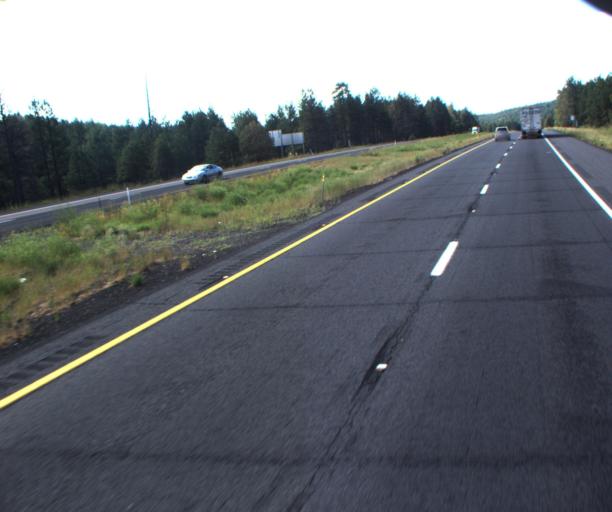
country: US
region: Arizona
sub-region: Coconino County
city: Mountainaire
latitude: 34.9658
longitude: -111.6819
